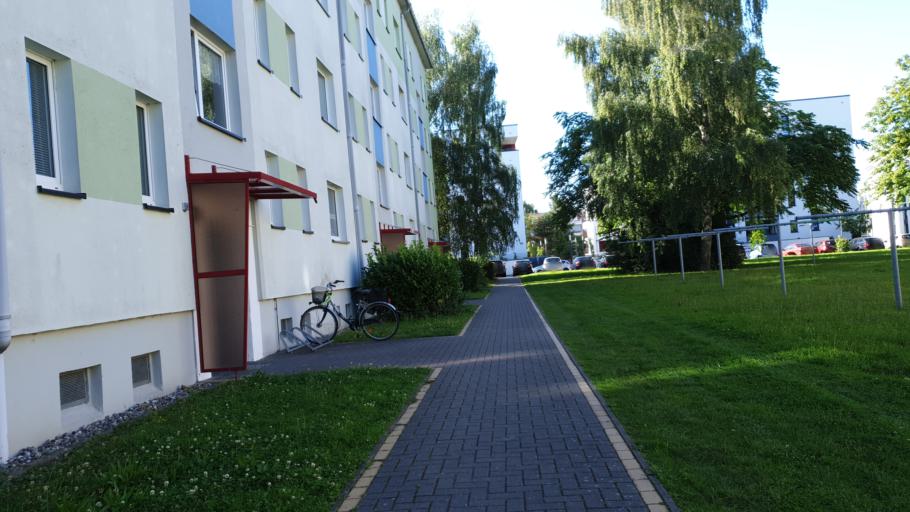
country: DE
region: Mecklenburg-Vorpommern
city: Stralsund
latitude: 54.3315
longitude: 13.0754
